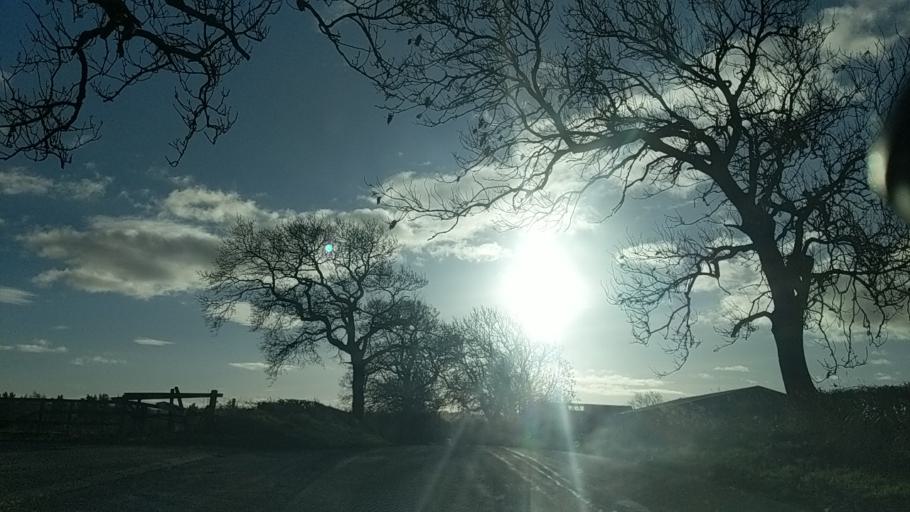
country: GB
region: Scotland
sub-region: West Lothian
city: Linlithgow
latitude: 55.9855
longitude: -3.5340
